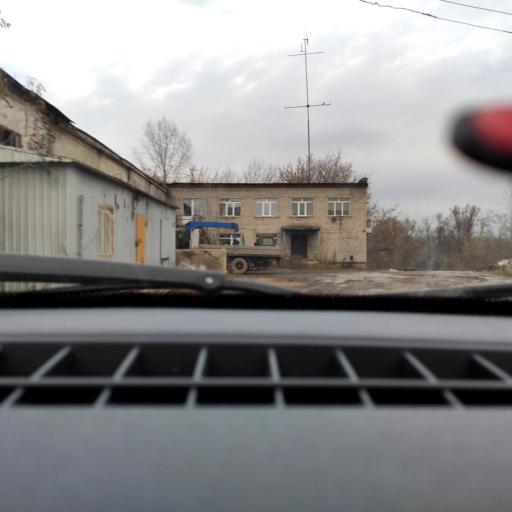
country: RU
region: Bashkortostan
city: Ufa
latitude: 54.6813
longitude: 55.9842
